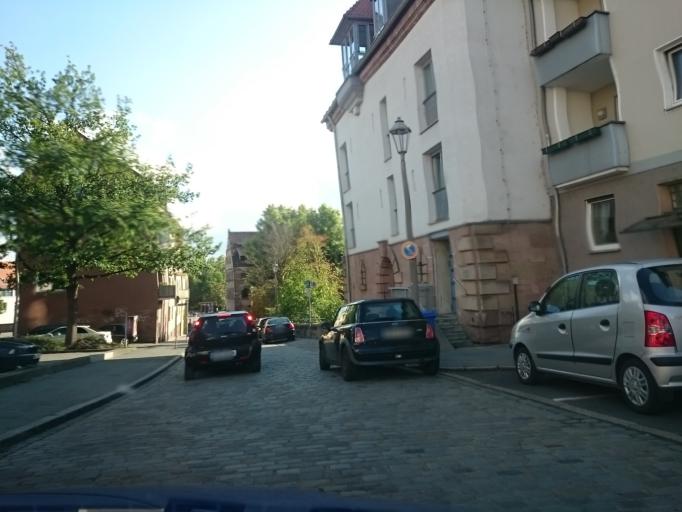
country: DE
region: Bavaria
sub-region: Regierungsbezirk Mittelfranken
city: Nuernberg
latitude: 49.4555
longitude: 11.0841
